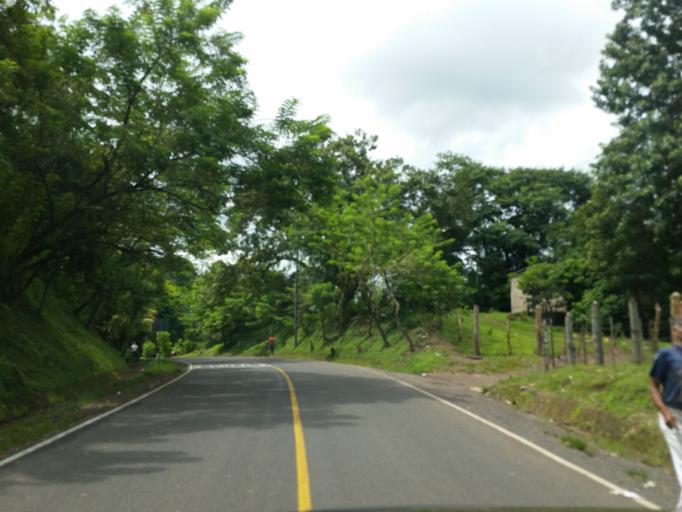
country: NI
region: Matagalpa
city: San Ramon
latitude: 13.1154
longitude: -85.7498
